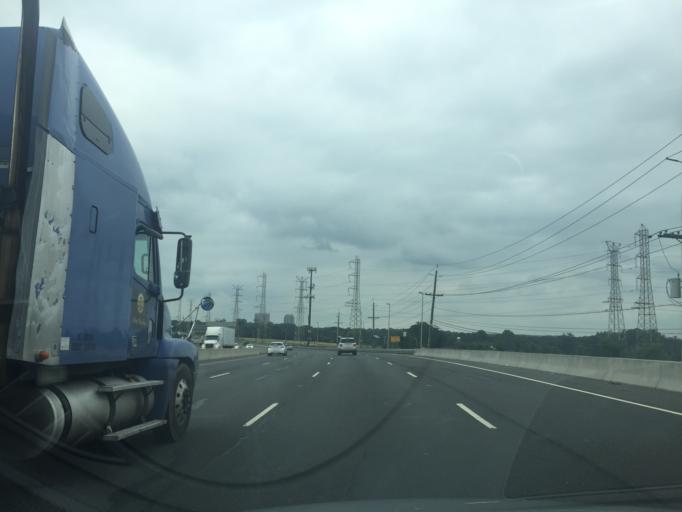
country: US
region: New Jersey
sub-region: Middlesex County
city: Milltown
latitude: 40.4673
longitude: -74.4379
